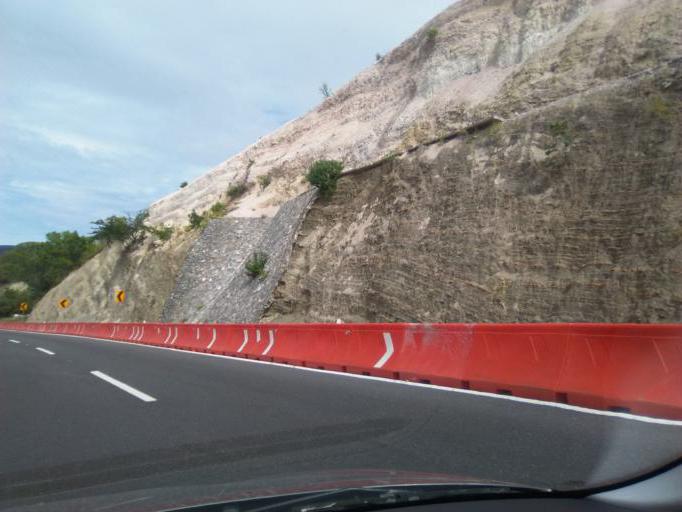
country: MX
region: Guerrero
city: Zumpango del Rio
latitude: 17.6343
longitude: -99.5050
